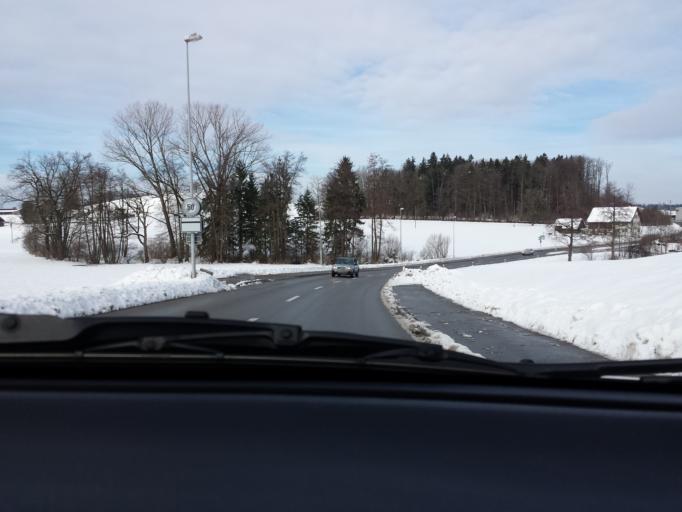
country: CH
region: Zurich
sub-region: Bezirk Hinwil
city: Bubikon
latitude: 47.2715
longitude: 8.8187
